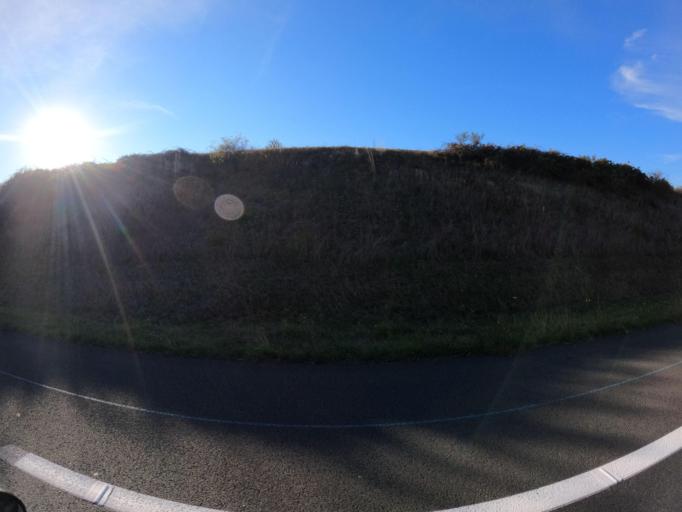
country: FR
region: Pays de la Loire
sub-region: Departement de Maine-et-Loire
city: Chemille-Melay
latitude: 47.2223
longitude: -0.7598
